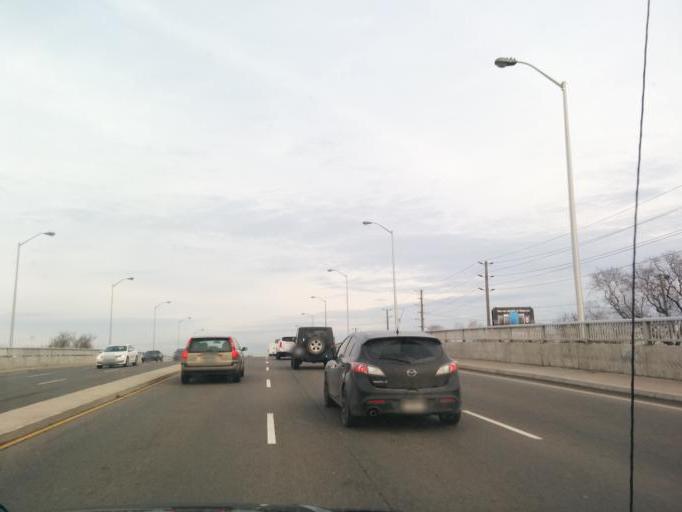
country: CA
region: Ontario
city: Etobicoke
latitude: 43.6196
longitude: -79.5325
